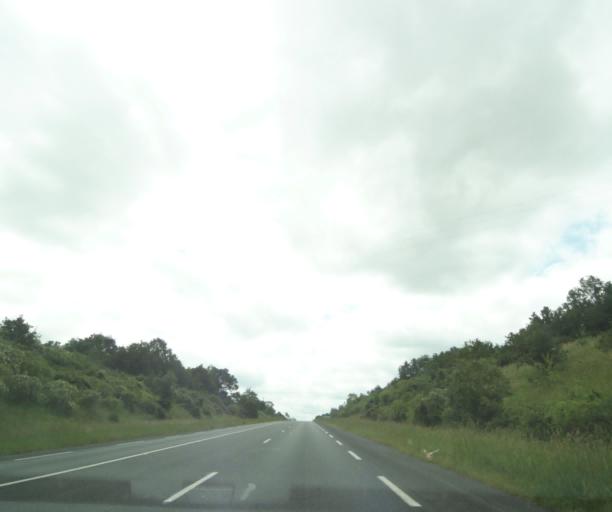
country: FR
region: Poitou-Charentes
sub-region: Departement des Deux-Sevres
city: Saint-Varent
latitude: 46.9116
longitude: -0.1944
